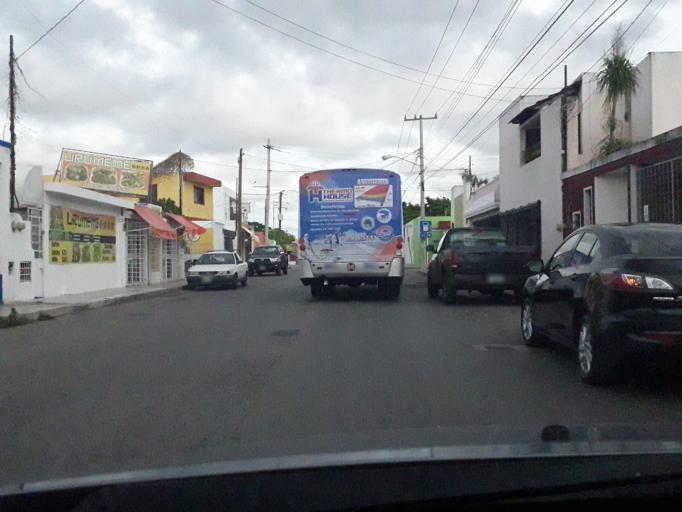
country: MX
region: Yucatan
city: Merida
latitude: 21.0209
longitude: -89.6395
